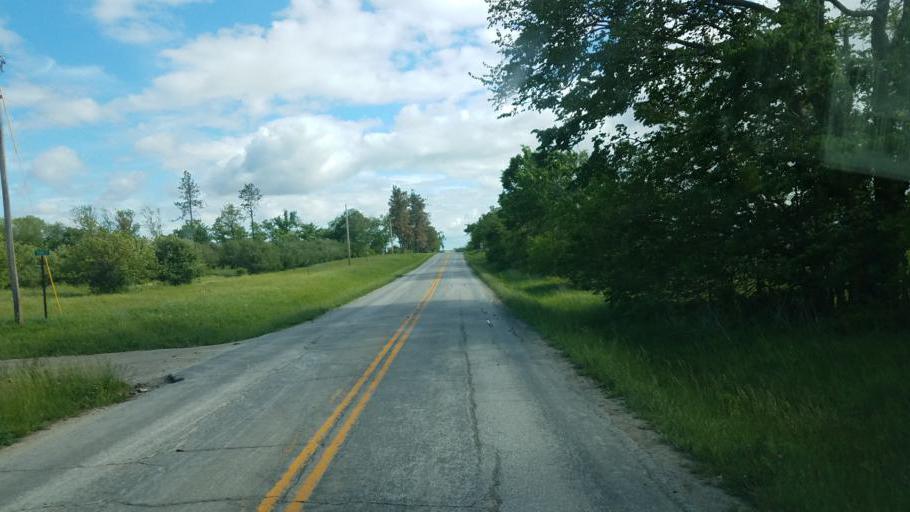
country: US
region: Missouri
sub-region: Mercer County
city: Princeton
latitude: 40.2532
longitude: -93.6757
